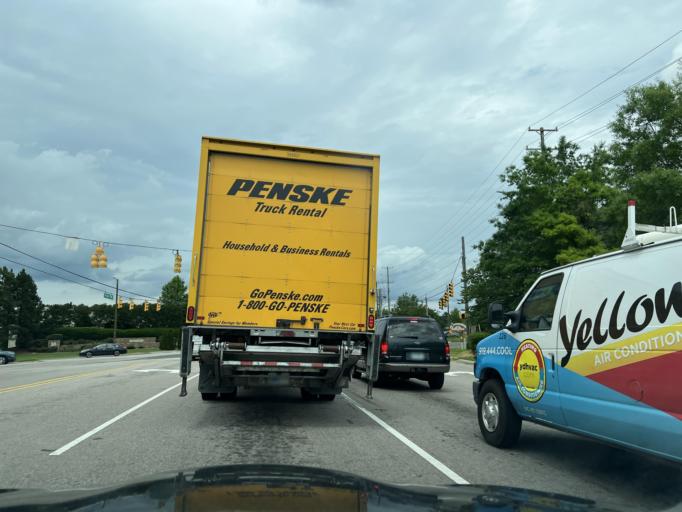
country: US
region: North Carolina
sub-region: Wake County
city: Morrisville
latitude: 35.9187
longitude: -78.8141
